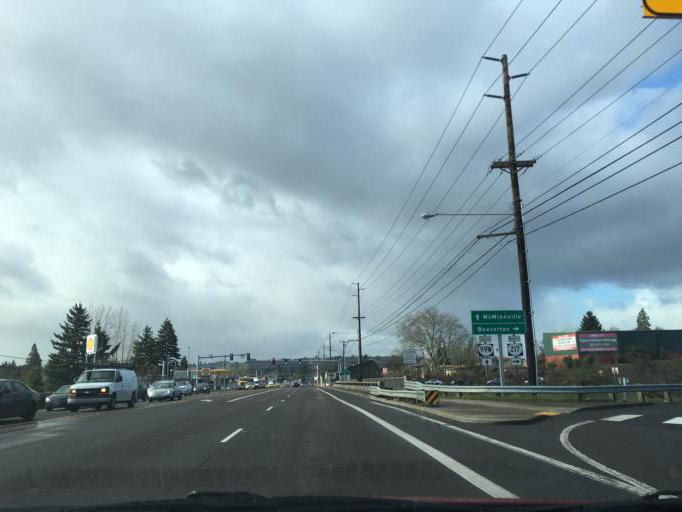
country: US
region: Oregon
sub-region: Washington County
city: Metzger
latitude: 45.4355
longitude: -122.7610
